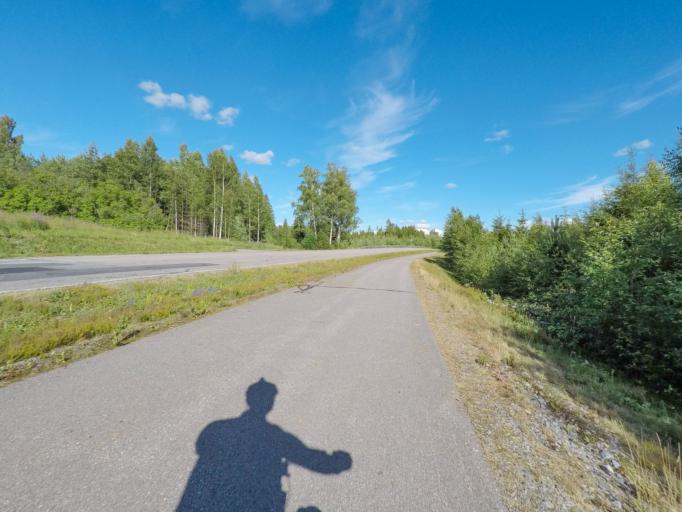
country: FI
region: South Karelia
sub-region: Lappeenranta
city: Joutseno
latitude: 61.1543
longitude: 28.6032
